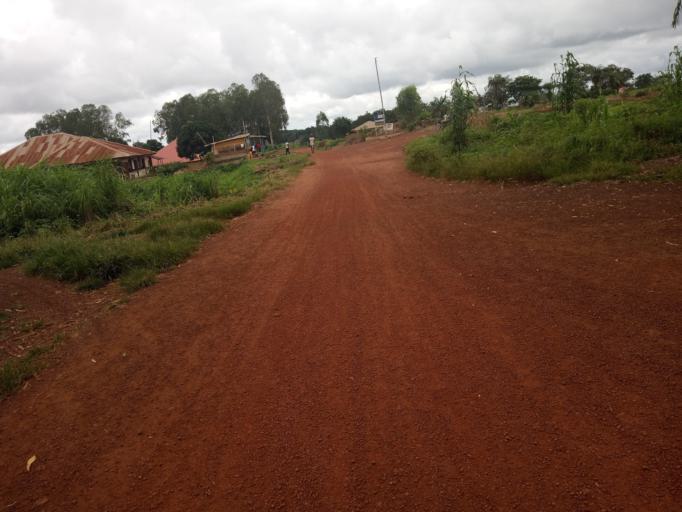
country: SL
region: Northern Province
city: Kamakwie
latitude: 9.5012
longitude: -12.2500
